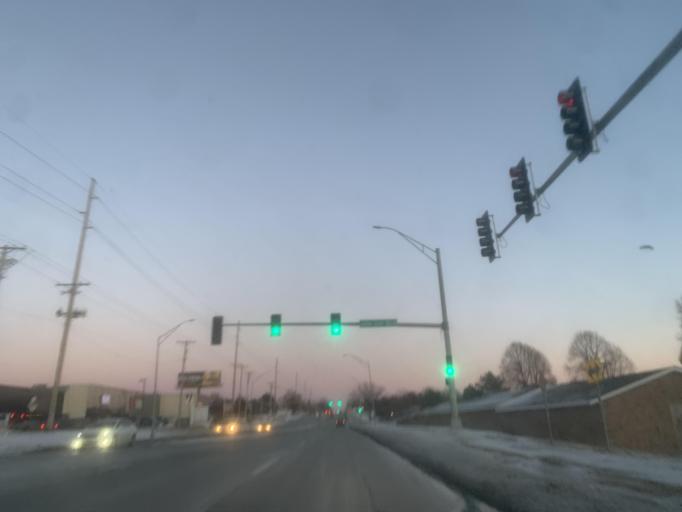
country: US
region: Nebraska
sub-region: Douglas County
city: Ralston
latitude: 41.2053
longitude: -96.0880
